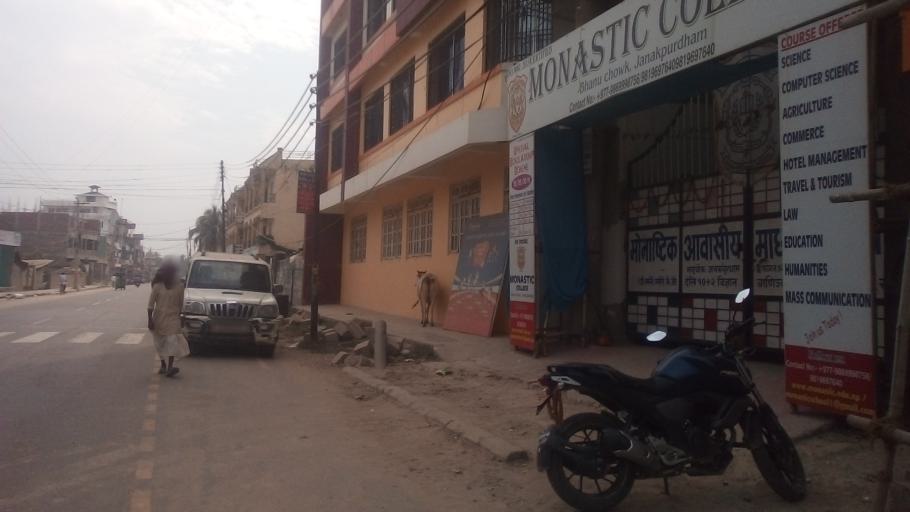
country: NP
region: Central Region
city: Janakpur
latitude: 26.7302
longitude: 85.9336
